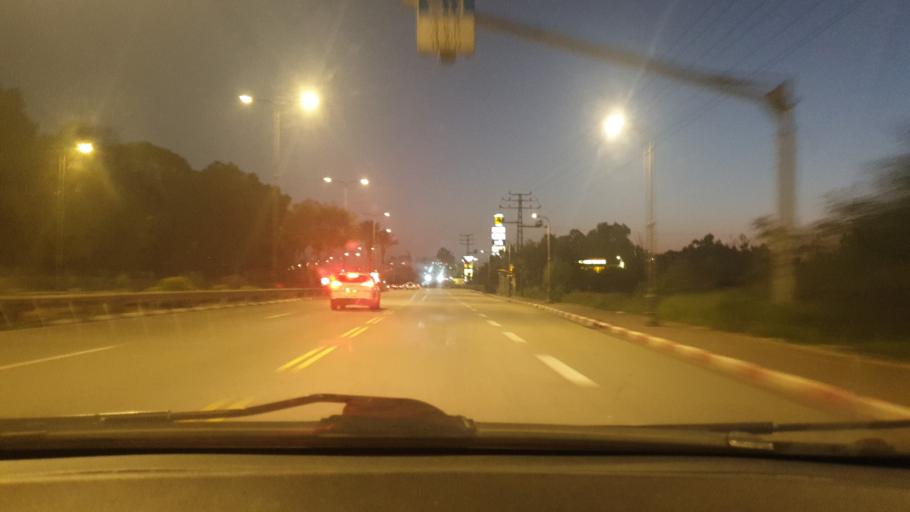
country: IL
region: Central District
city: Bet Dagan
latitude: 31.9929
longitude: 34.8136
